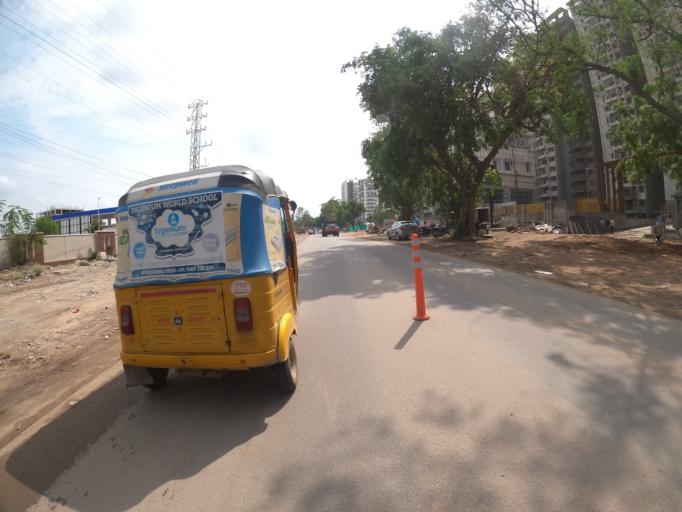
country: IN
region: Telangana
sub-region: Medak
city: Serilingampalle
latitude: 17.3879
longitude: 78.3419
